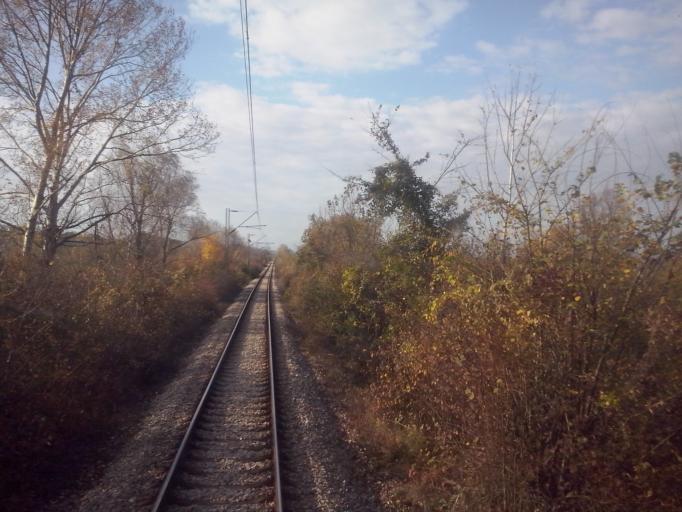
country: RS
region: Central Serbia
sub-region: Belgrade
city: Lazarevac
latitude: 44.4121
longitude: 20.2697
